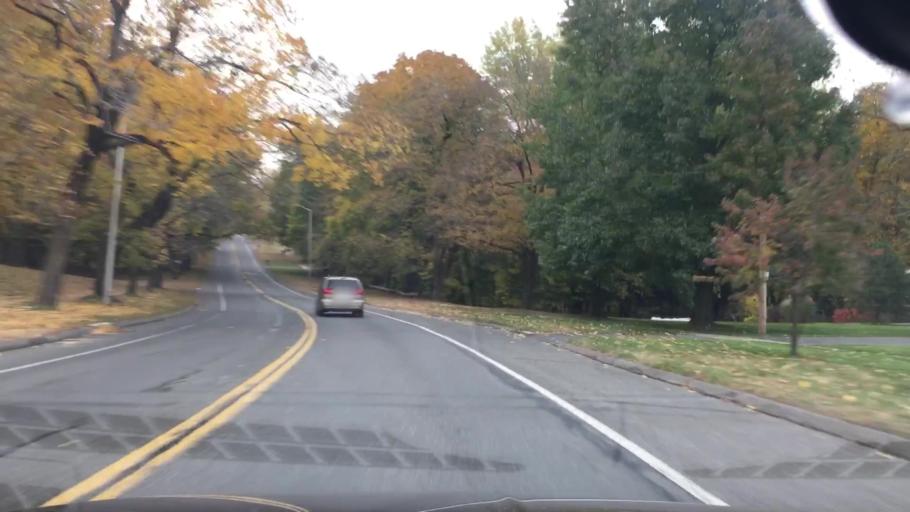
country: US
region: Massachusetts
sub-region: Hampden County
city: Longmeadow
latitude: 42.0291
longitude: -72.5812
